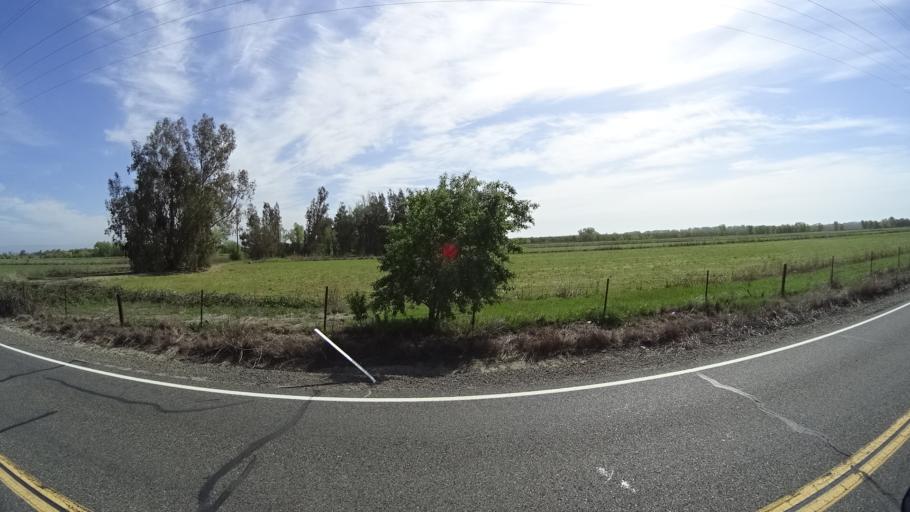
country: US
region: California
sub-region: Glenn County
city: Hamilton City
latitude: 39.6835
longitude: -122.0052
